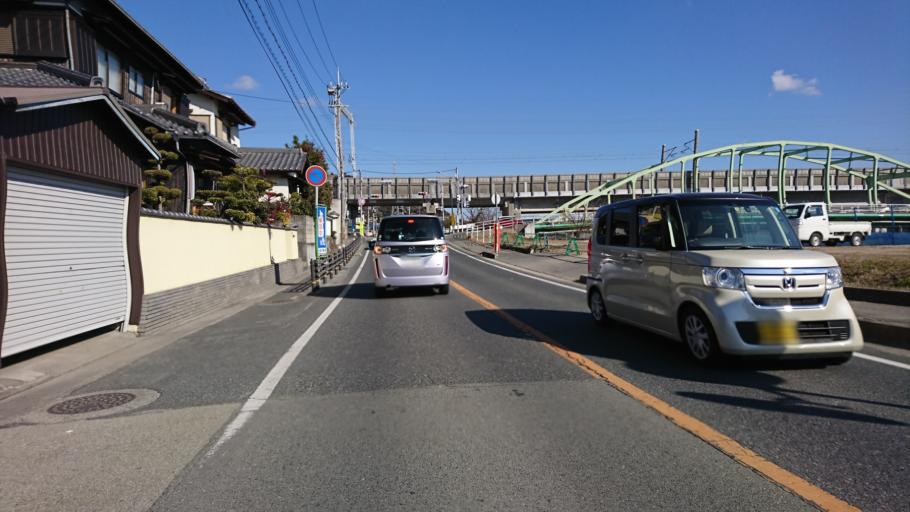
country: JP
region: Hyogo
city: Kakogawacho-honmachi
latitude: 34.7706
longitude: 134.7931
